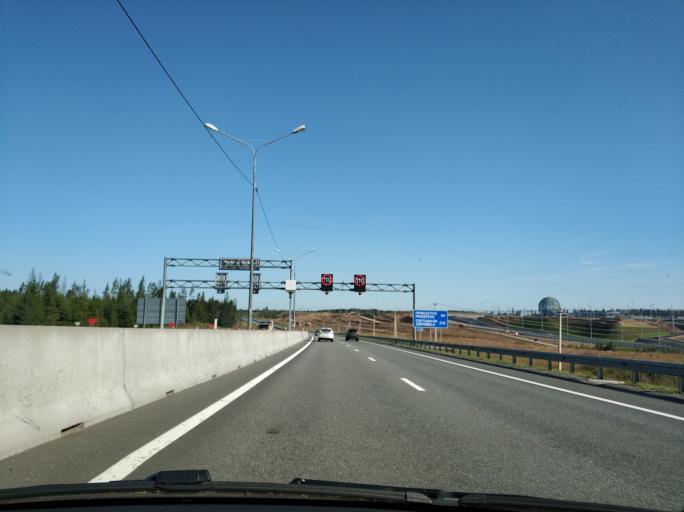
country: RU
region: Leningrad
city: Sosnovo
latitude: 60.5041
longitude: 30.1941
